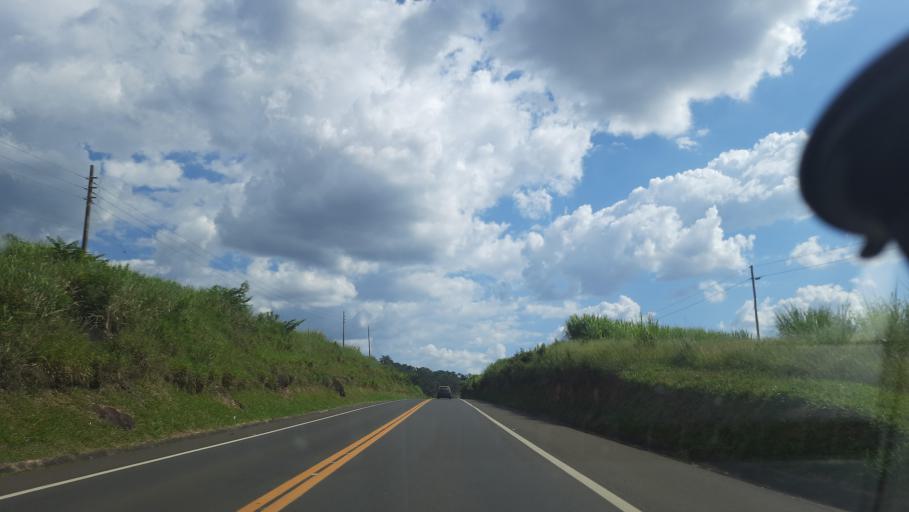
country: BR
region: Sao Paulo
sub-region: Sao Jose Do Rio Pardo
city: Sao Jose do Rio Pardo
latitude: -21.6454
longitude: -46.9082
